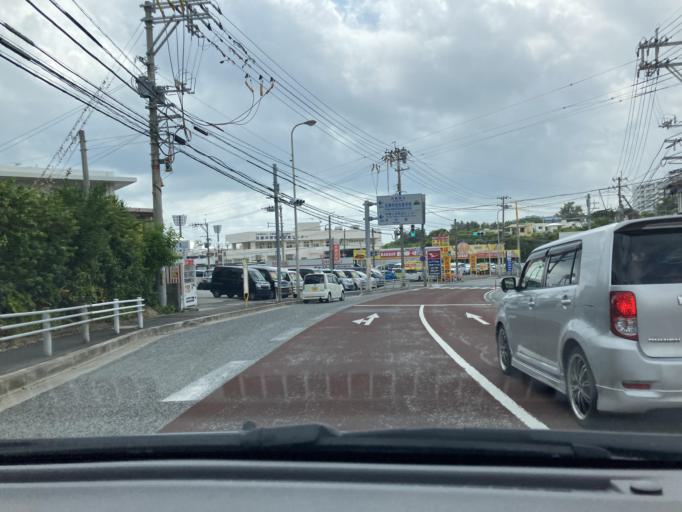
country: JP
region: Okinawa
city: Okinawa
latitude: 26.3145
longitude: 127.8190
